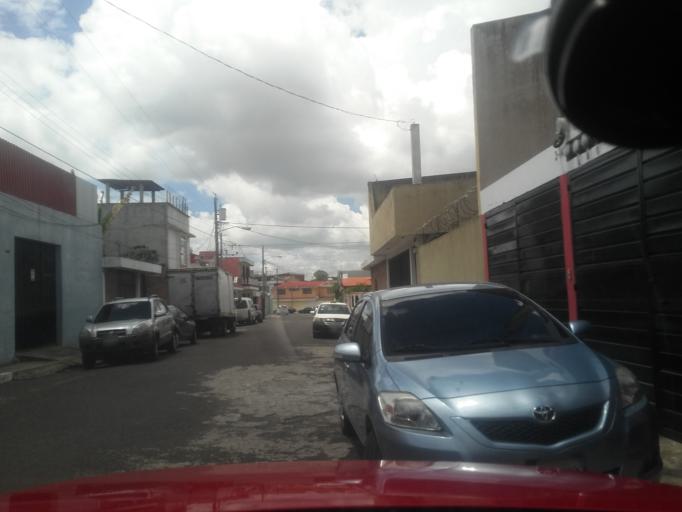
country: GT
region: Guatemala
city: Mixco
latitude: 14.6434
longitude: -90.5669
